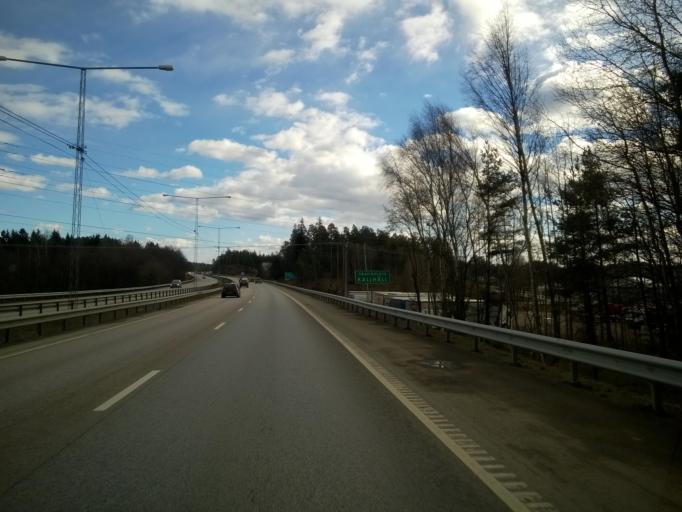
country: SE
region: Stockholm
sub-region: Jarfalla Kommun
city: Jakobsberg
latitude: 59.4576
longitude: 17.8280
